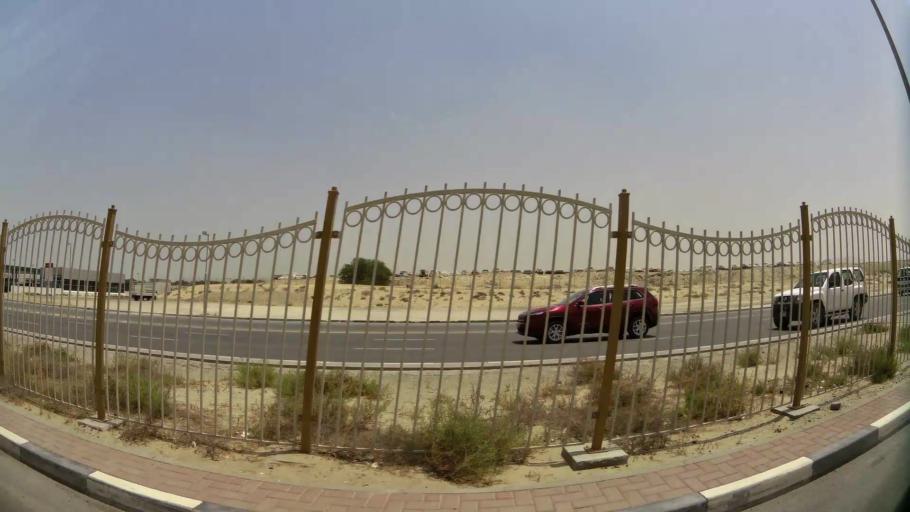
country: AE
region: Ash Shariqah
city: Sharjah
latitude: 25.2820
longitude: 55.4122
